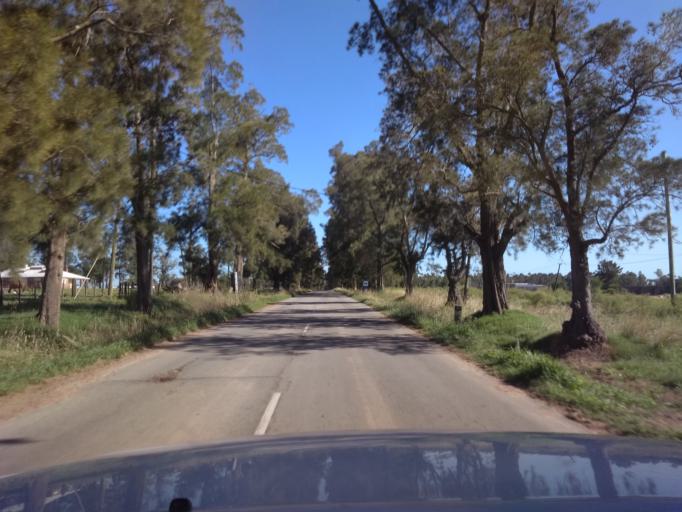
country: UY
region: Canelones
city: San Bautista
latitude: -34.3861
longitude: -55.9595
